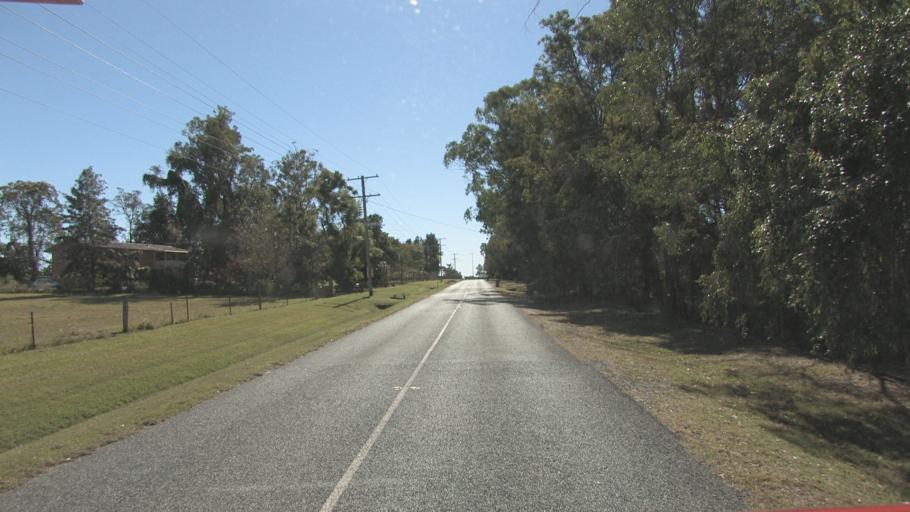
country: AU
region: Queensland
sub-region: Logan
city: Park Ridge South
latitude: -27.7091
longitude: 153.0585
